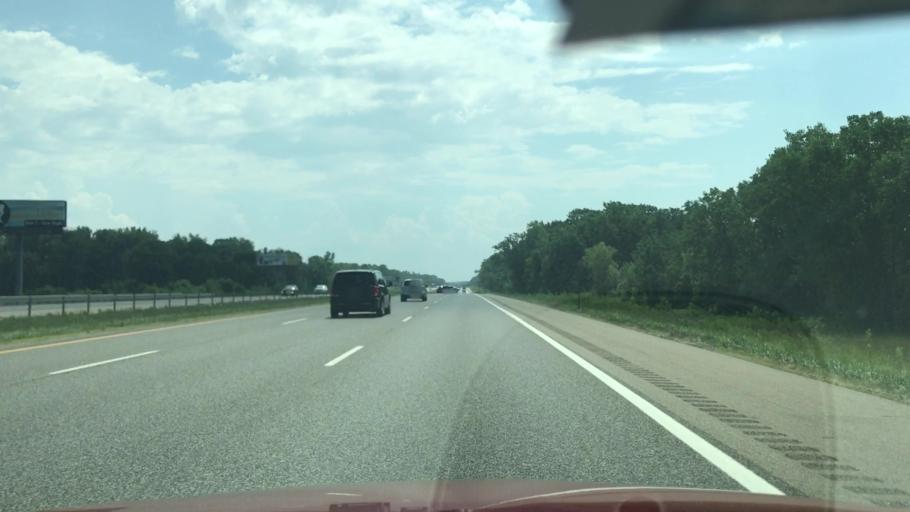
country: US
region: Michigan
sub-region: Berrien County
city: Bridgman
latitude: 41.9139
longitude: -86.5773
